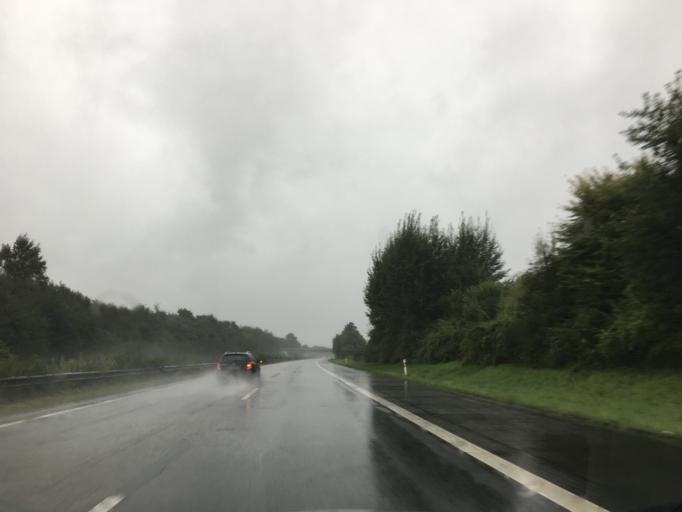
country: DE
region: Schleswig-Holstein
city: Rumohr
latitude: 54.2637
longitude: 10.0413
